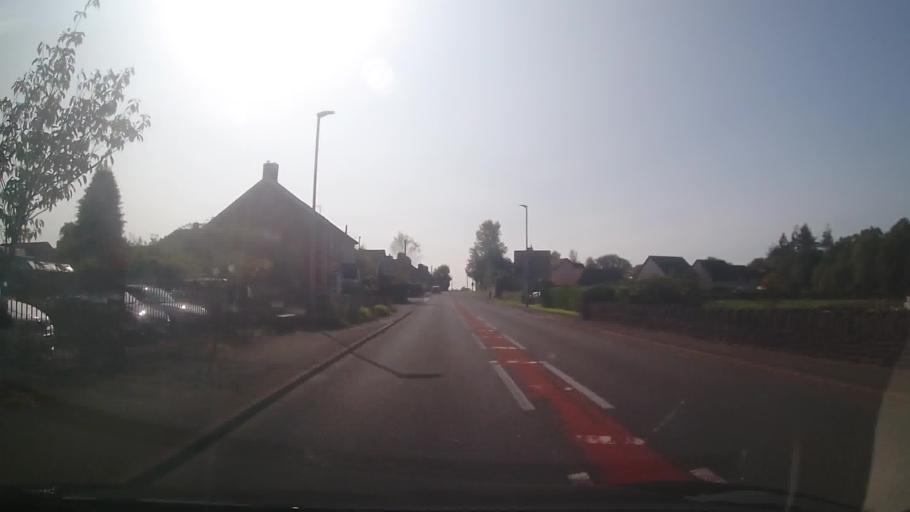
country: GB
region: Wales
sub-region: Sir Powys
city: Llandrindod Wells
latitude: 52.2122
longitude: -3.4407
